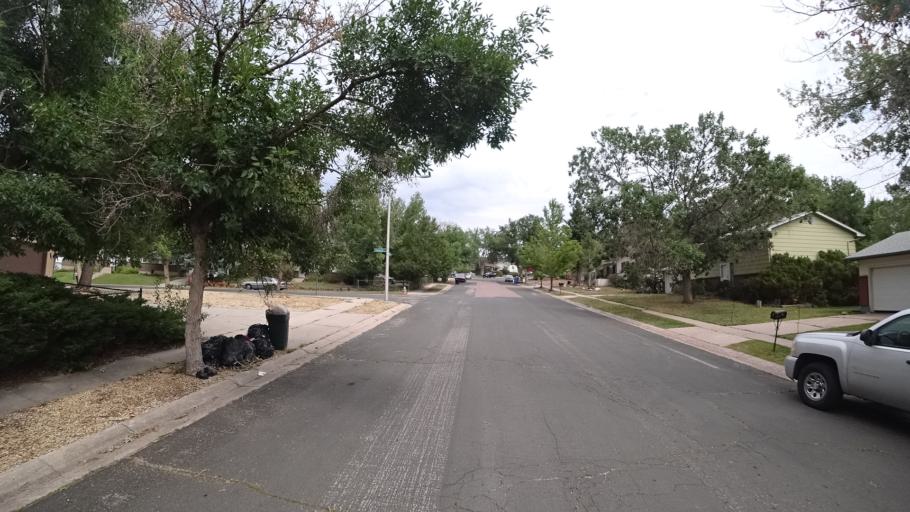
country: US
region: Colorado
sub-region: El Paso County
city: Colorado Springs
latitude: 38.8960
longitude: -104.8114
